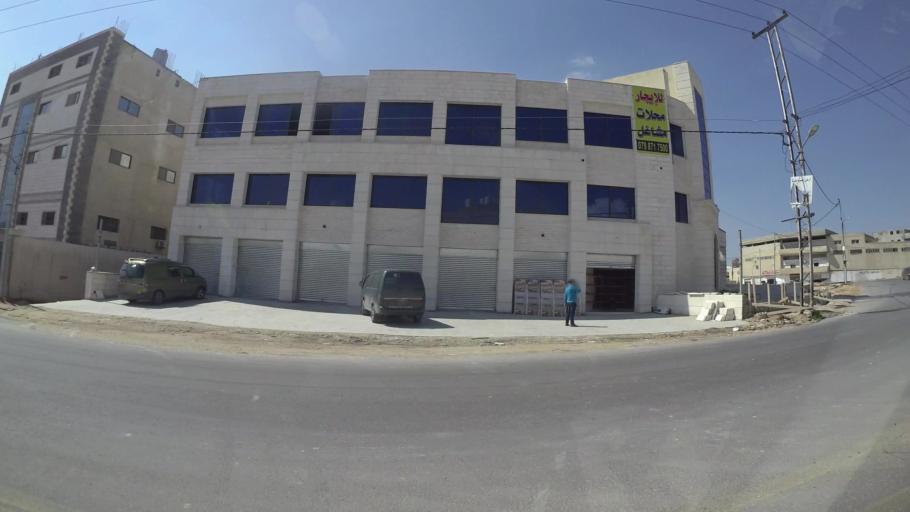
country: JO
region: Zarqa
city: Russeifa
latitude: 31.9919
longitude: 36.0129
